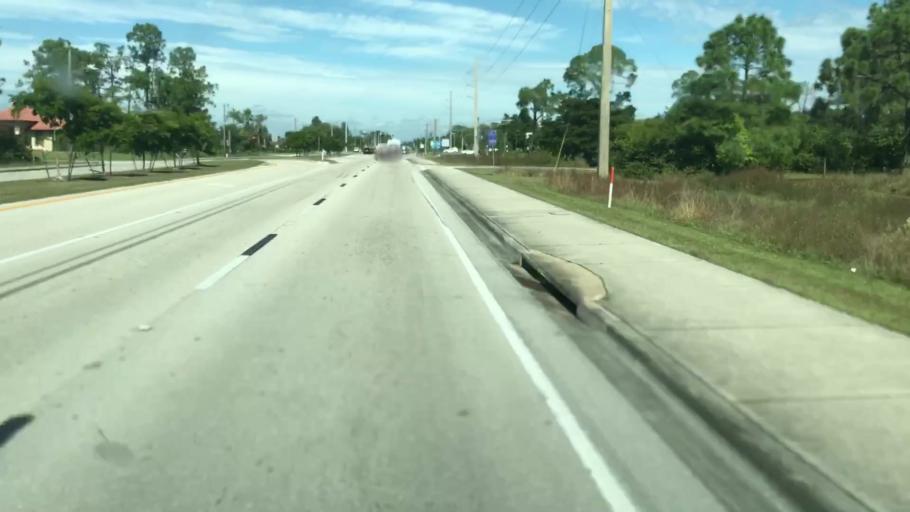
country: US
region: Florida
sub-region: Lee County
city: Gateway
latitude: 26.6144
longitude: -81.7144
